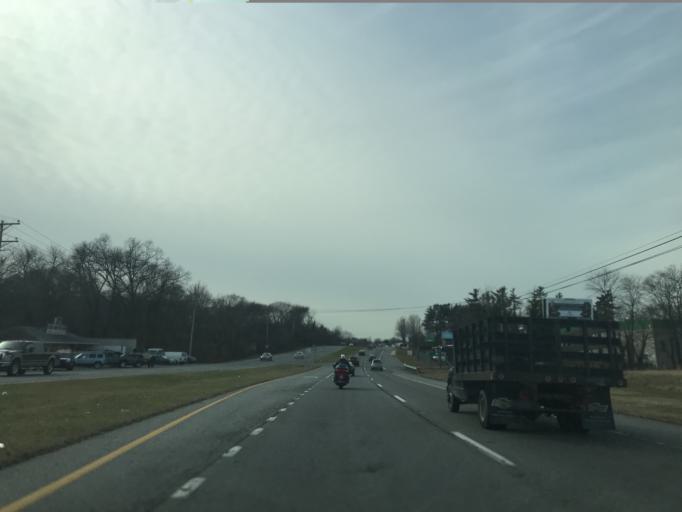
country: US
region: Delaware
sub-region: New Castle County
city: Bear
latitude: 39.6498
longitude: -75.6255
